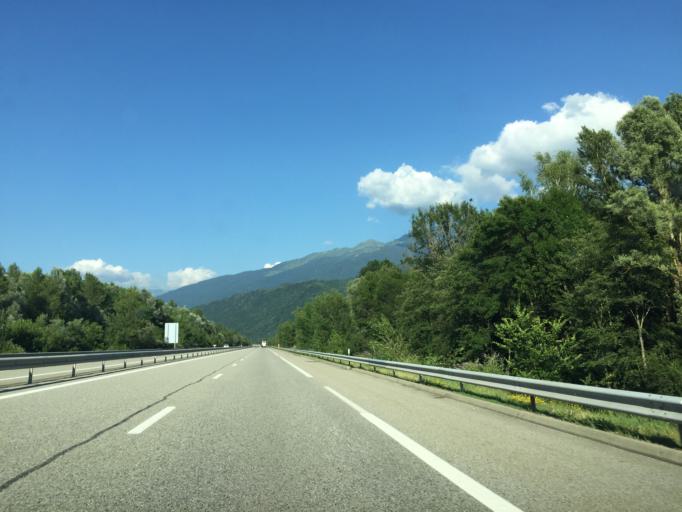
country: FR
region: Rhone-Alpes
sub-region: Departement de la Savoie
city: Aiton
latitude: 45.5762
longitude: 6.2517
